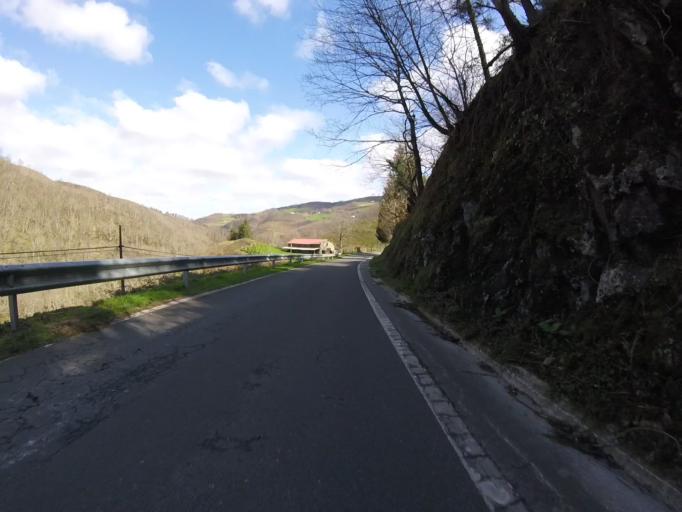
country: ES
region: Navarre
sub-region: Provincia de Navarra
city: Goizueta
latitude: 43.1486
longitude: -1.8515
